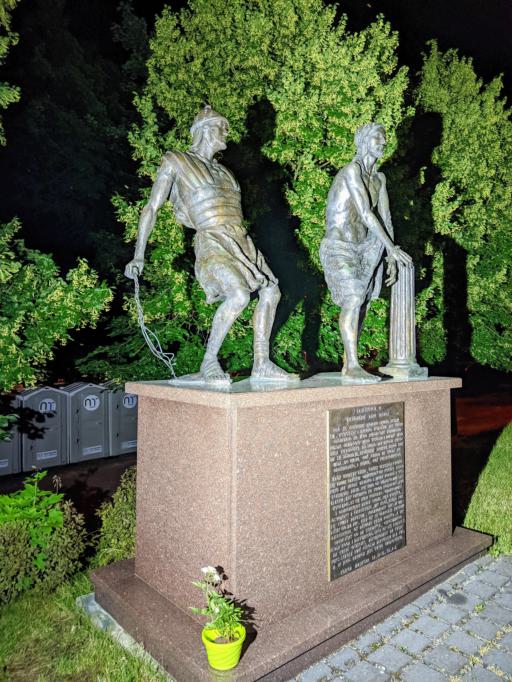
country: PL
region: Silesian Voivodeship
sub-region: Czestochowa
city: Czestochowa
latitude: 50.8120
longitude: 19.0999
